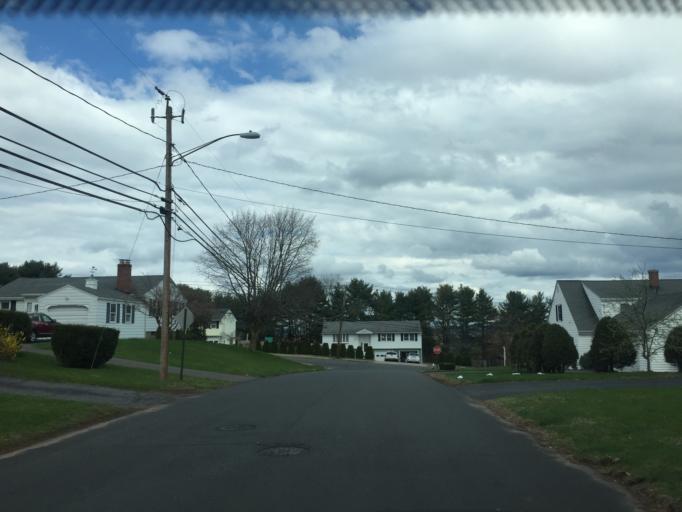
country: US
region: Connecticut
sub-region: Hartford County
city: New Britain
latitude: 41.7104
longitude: -72.7774
